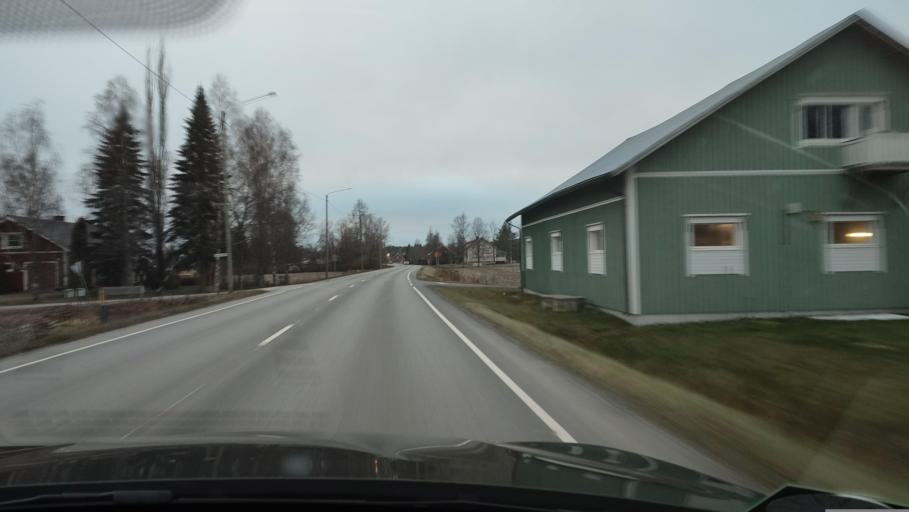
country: FI
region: Southern Ostrobothnia
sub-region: Suupohja
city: Karijoki
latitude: 62.3125
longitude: 21.7160
